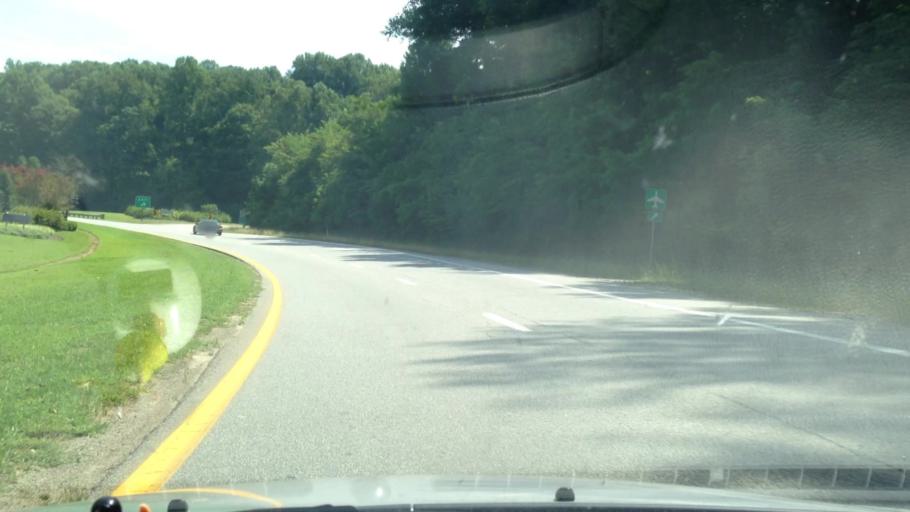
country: US
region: Virginia
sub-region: City of Martinsville
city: Martinsville
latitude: 36.6632
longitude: -79.8832
